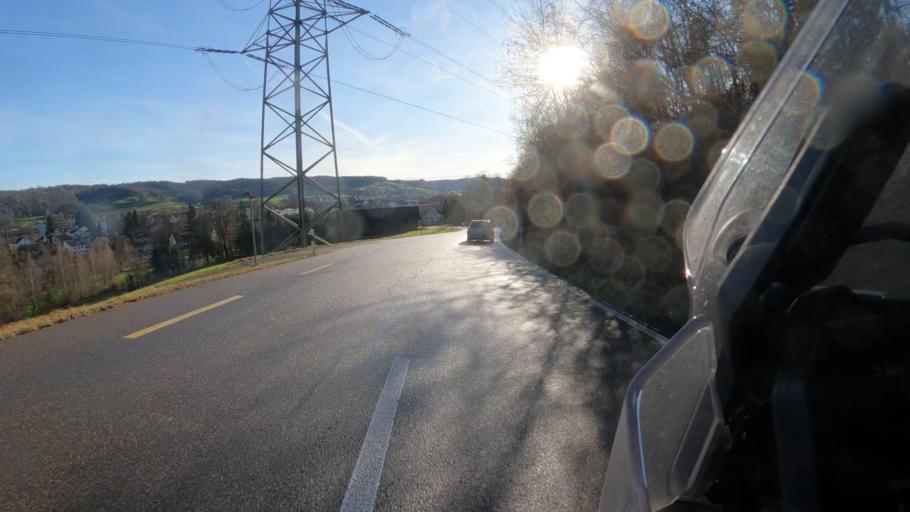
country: CH
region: Zurich
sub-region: Bezirk Buelach
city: Embrach / Kellersacker
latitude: 47.5143
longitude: 8.5840
